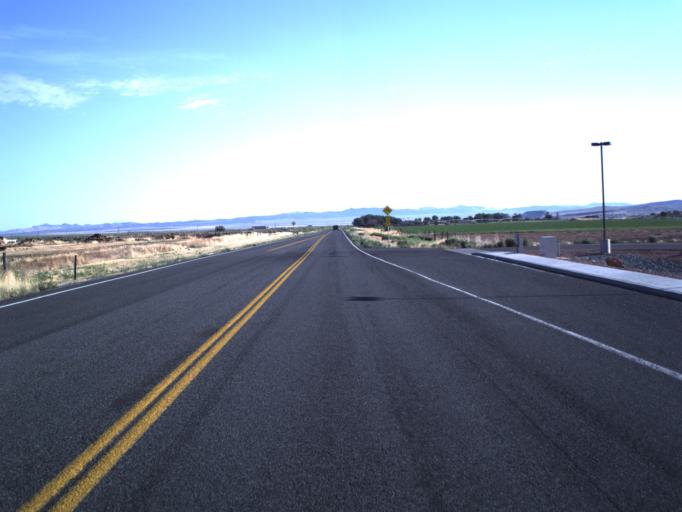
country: US
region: Utah
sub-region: Iron County
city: Enoch
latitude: 37.7651
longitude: -113.0552
